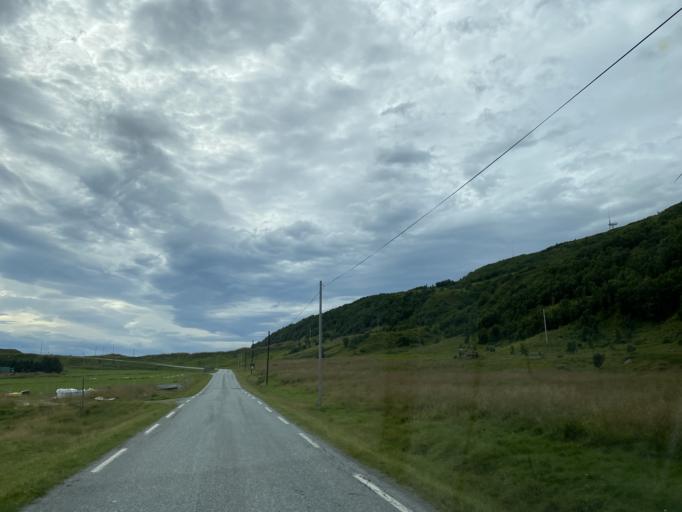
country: NO
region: Troms
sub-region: Karlsoy
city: Hansnes
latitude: 70.0957
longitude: 20.0895
